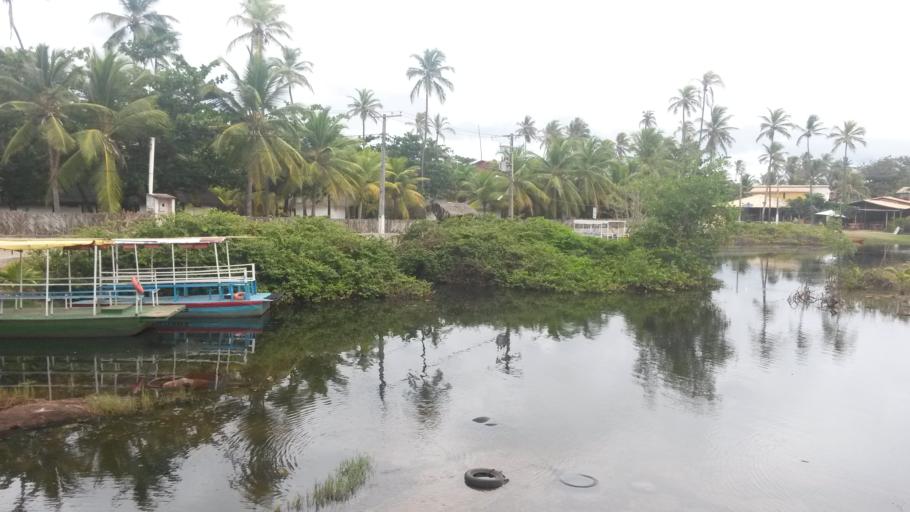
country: BR
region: Bahia
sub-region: Mata De Sao Joao
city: Mata de Sao Joao
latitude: -12.4957
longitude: -37.9591
